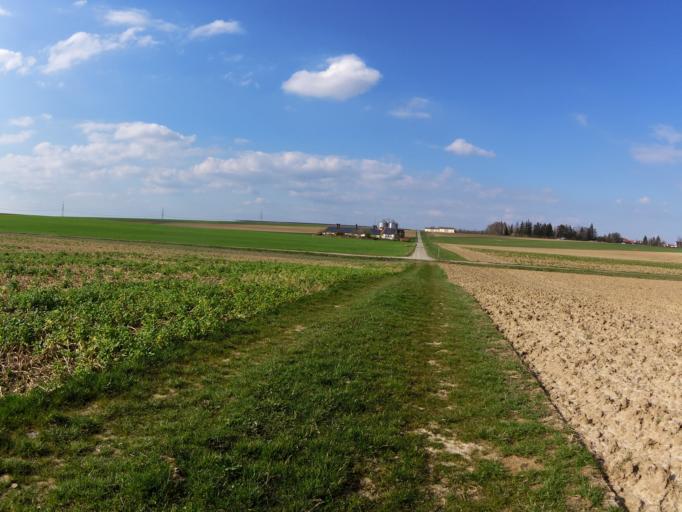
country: DE
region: Bavaria
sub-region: Regierungsbezirk Unterfranken
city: Biebelried
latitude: 49.7894
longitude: 10.0813
